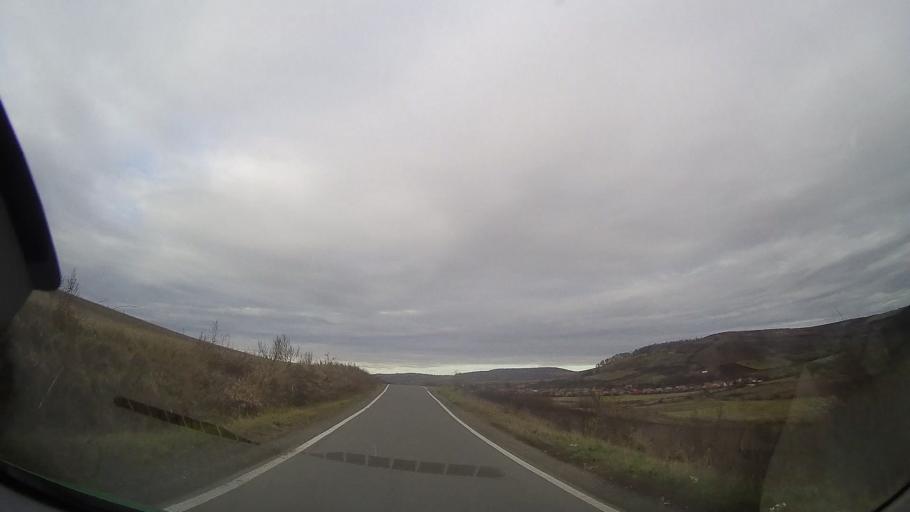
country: RO
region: Mures
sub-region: Comuna Faragau
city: Faragau
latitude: 46.7701
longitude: 24.5573
